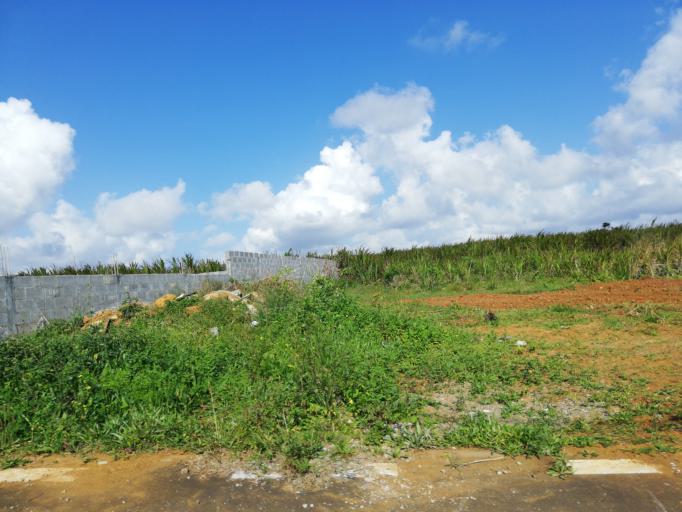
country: MU
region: Moka
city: Verdun
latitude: -20.2265
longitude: 57.5489
